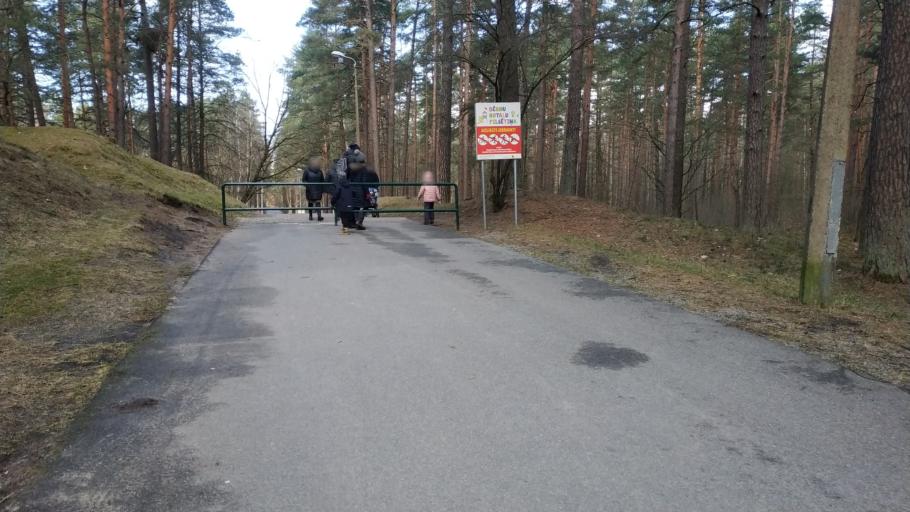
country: LV
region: Riga
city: Jaunciems
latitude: 57.0085
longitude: 24.1520
